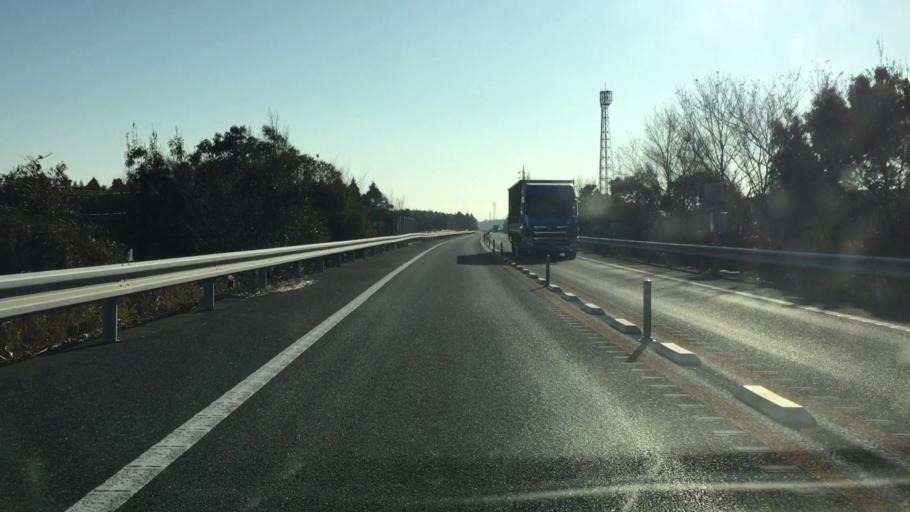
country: JP
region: Ibaraki
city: Ami
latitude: 35.9935
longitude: 140.2145
